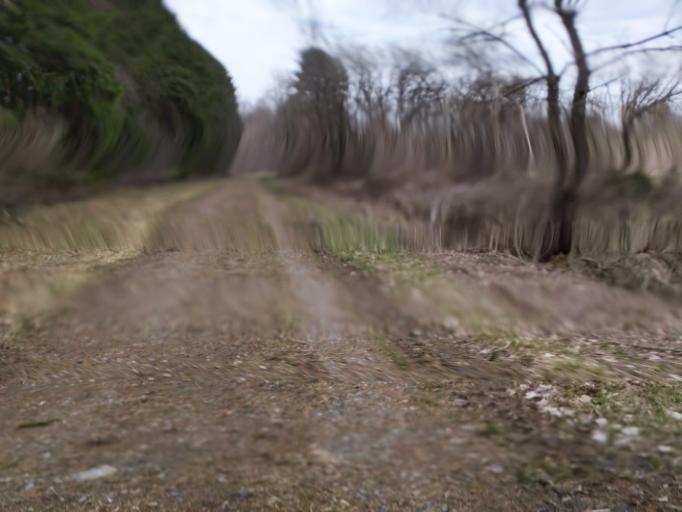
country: US
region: New York
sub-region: Tompkins County
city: Dryden
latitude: 42.5008
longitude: -76.3351
